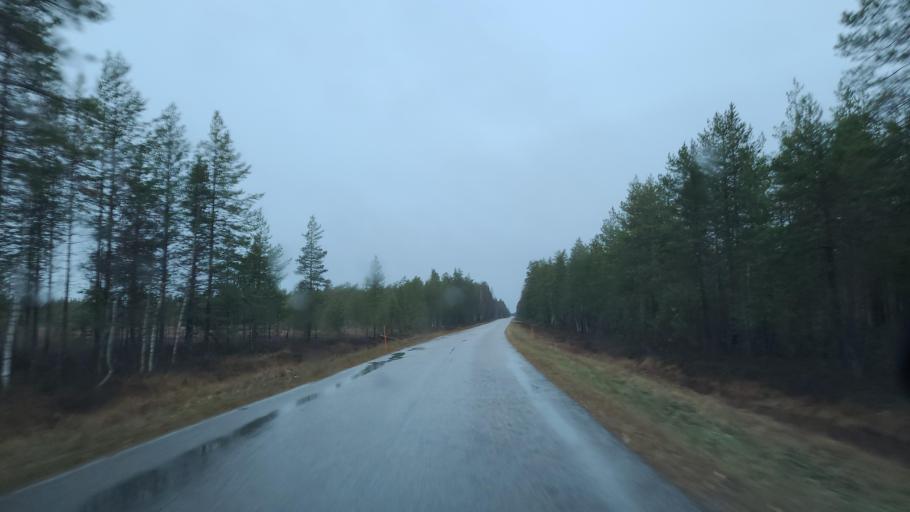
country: FI
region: Lapland
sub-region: Kemi-Tornio
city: Simo
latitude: 65.8678
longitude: 25.2233
